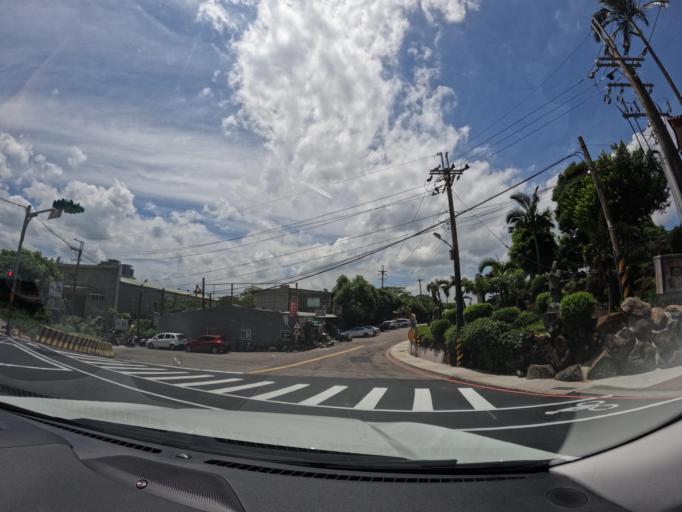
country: TW
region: Taiwan
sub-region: Taoyuan
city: Taoyuan
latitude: 25.0470
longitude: 121.3825
